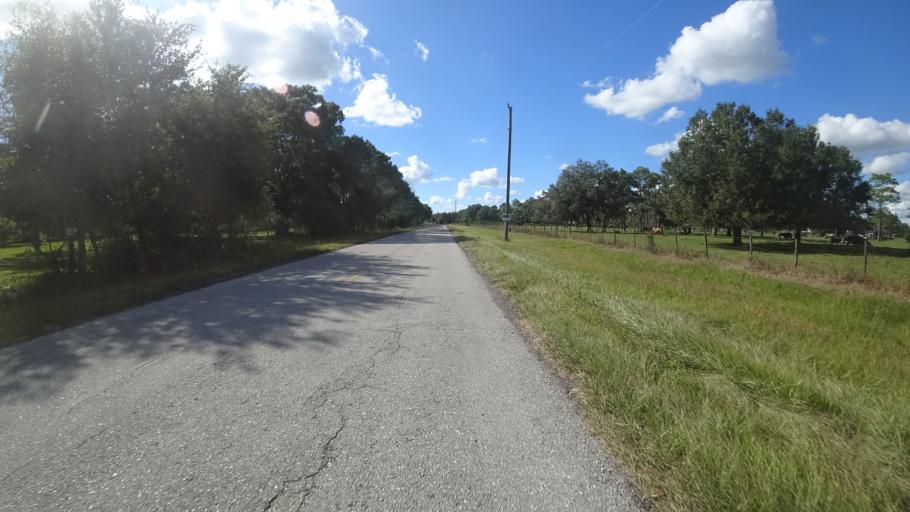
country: US
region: Florida
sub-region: Sarasota County
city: Warm Mineral Springs
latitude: 27.2740
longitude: -82.1167
